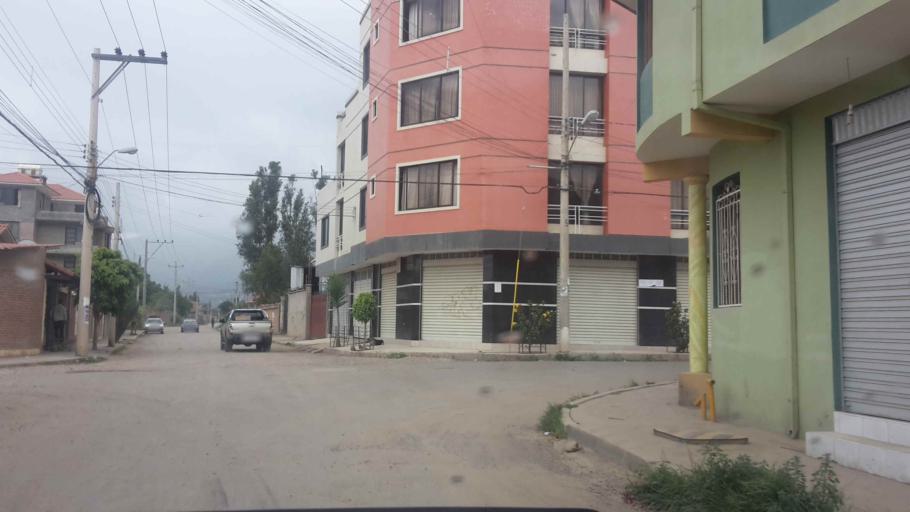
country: BO
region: Cochabamba
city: Cochabamba
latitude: -17.3395
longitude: -66.2224
